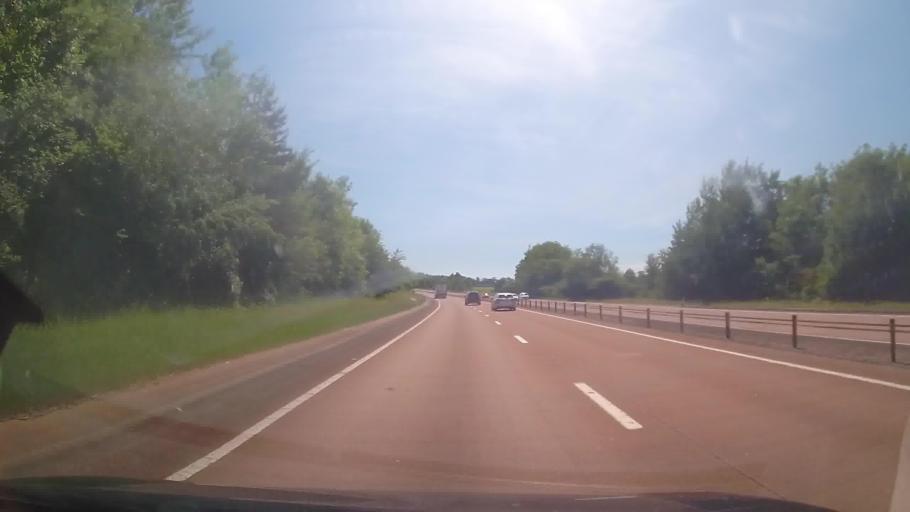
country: GB
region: England
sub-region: Devon
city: Newton Poppleford
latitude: 50.7427
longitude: -3.3607
